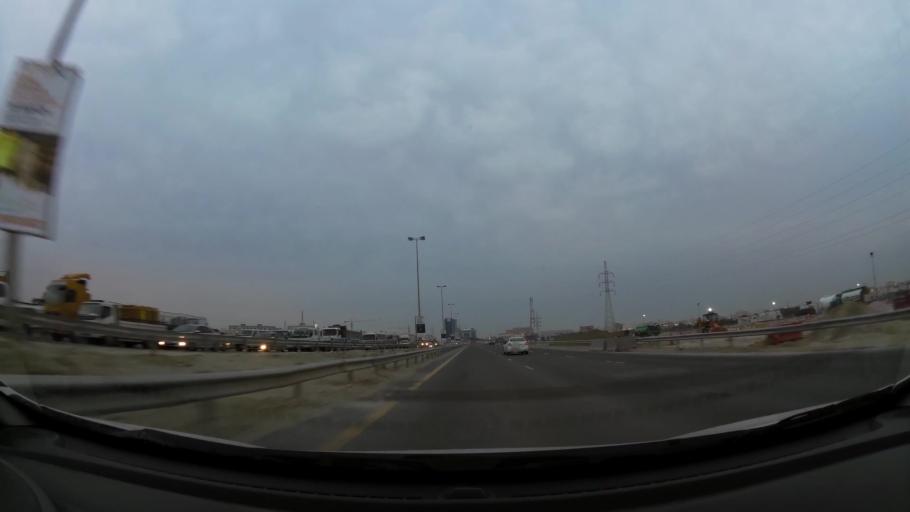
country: BH
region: Northern
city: Ar Rifa'
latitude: 26.1288
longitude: 50.5881
